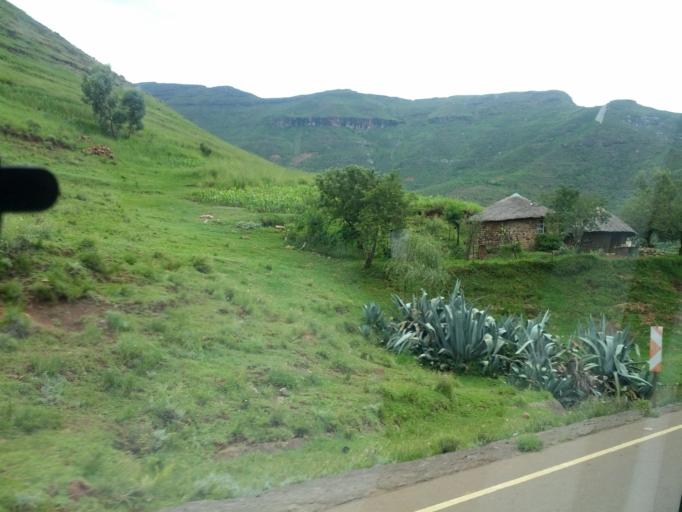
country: LS
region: Butha-Buthe
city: Butha-Buthe
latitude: -29.0445
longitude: 28.3176
